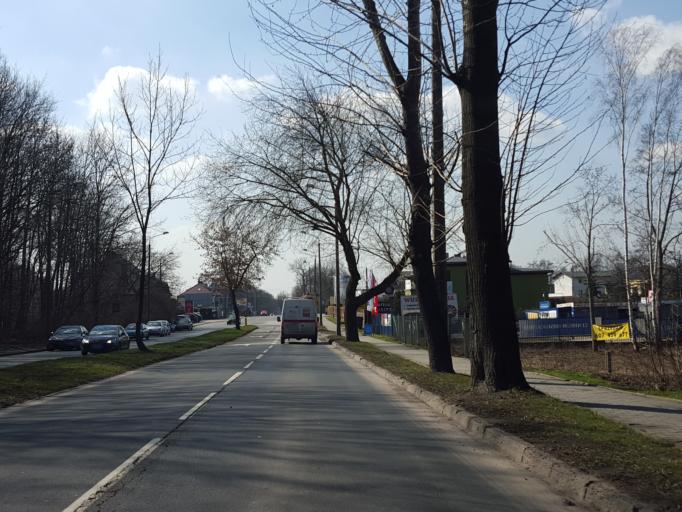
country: PL
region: Silesian Voivodeship
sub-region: Ruda Slaska
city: Ruda Slaska
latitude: 50.2513
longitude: 18.8498
